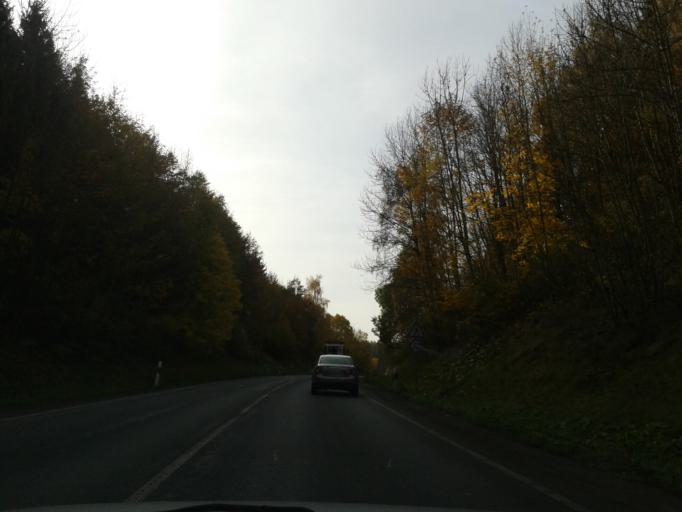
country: DE
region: North Rhine-Westphalia
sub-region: Regierungsbezirk Arnsberg
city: Ruthen
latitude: 51.4702
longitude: 8.4460
